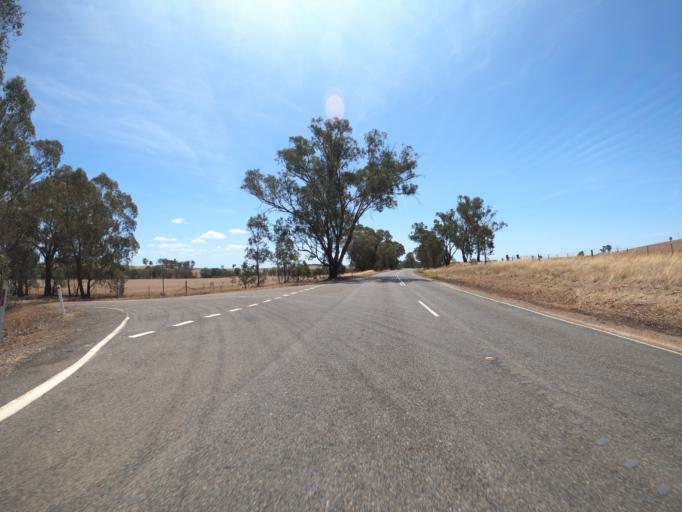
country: AU
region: Victoria
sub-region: Benalla
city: Benalla
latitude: -36.3426
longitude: 145.9591
